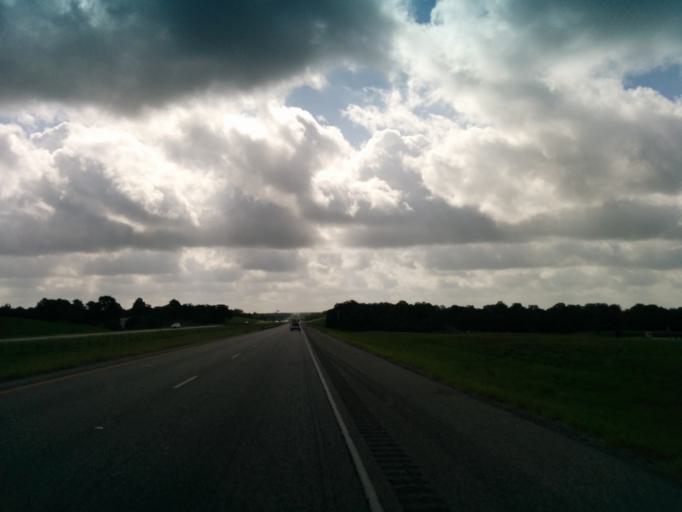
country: US
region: Texas
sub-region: Caldwell County
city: Luling
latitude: 29.6528
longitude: -97.5483
